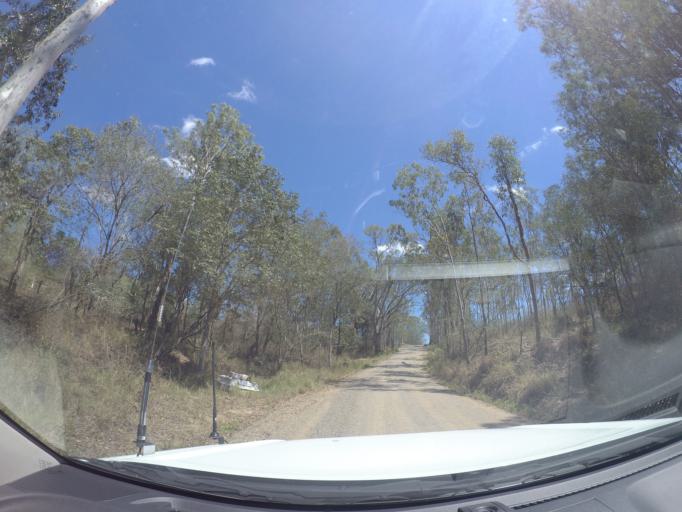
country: AU
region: Queensland
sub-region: Logan
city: North Maclean
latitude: -27.8372
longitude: 152.8715
